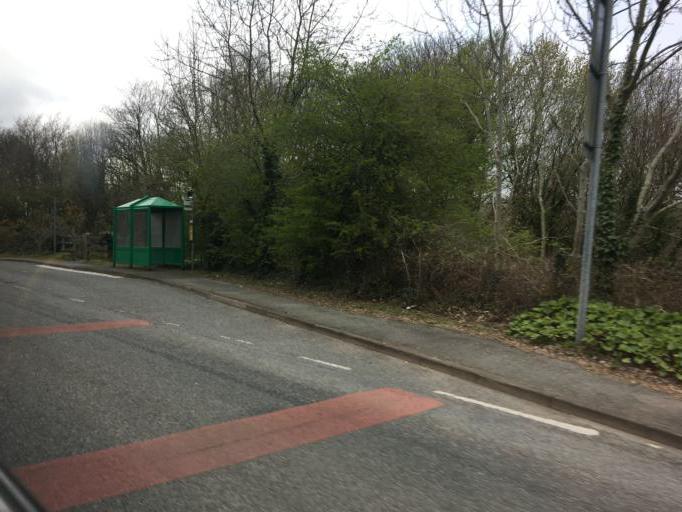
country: GB
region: Wales
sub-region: Gwynedd
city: Y Felinheli
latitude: 53.1748
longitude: -4.2242
